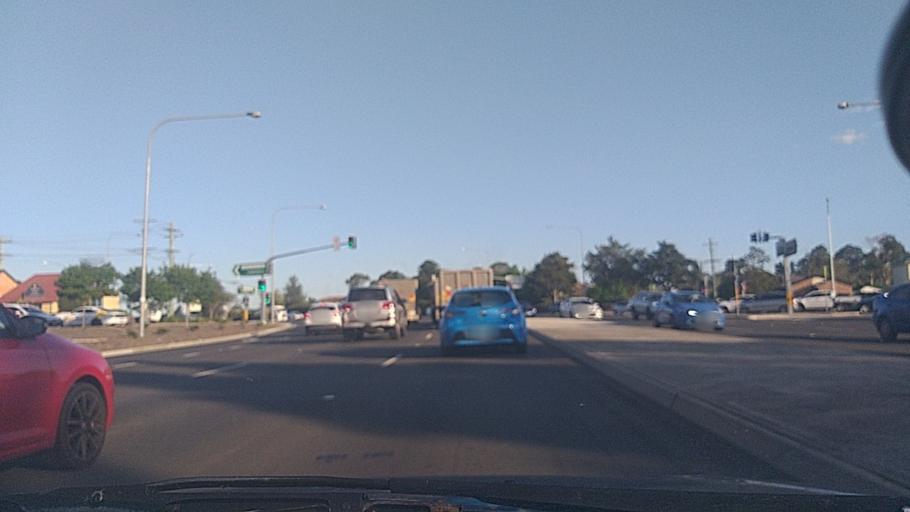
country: AU
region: New South Wales
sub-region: Camden
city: Narellan
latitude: -34.0388
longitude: 150.7391
